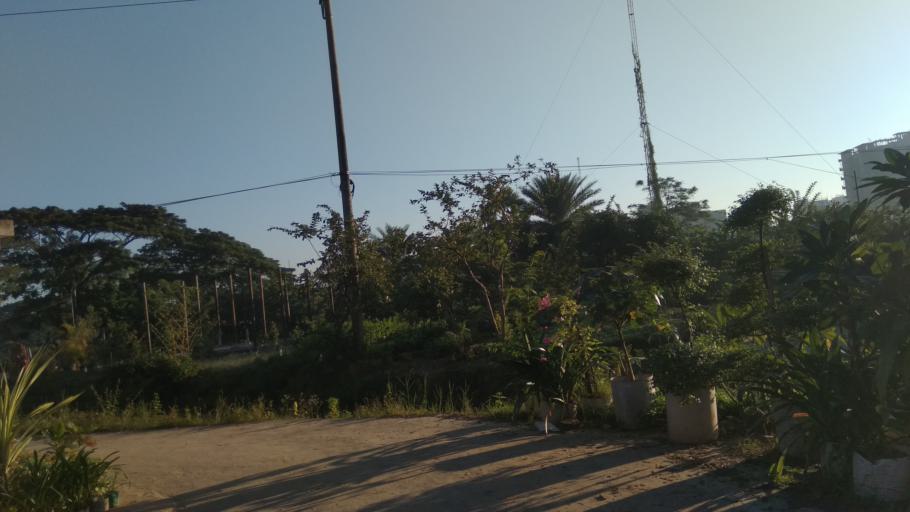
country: BD
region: Dhaka
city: Tungi
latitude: 23.8403
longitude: 90.4187
